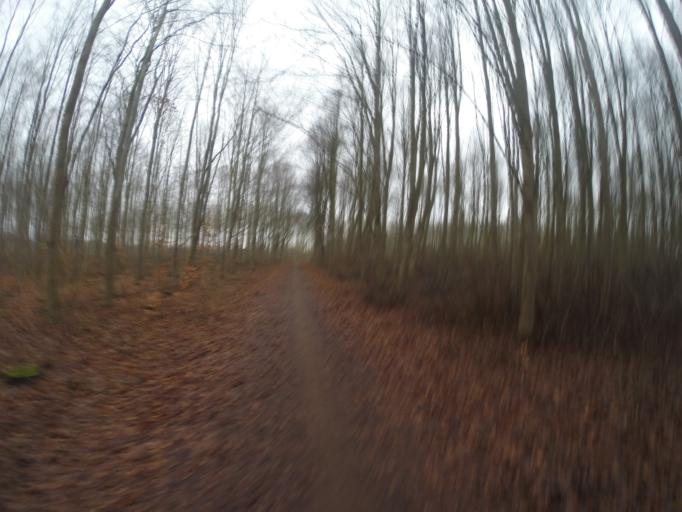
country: DK
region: Capital Region
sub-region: Hoje-Taastrup Kommune
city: Taastrup
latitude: 55.6882
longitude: 12.3221
